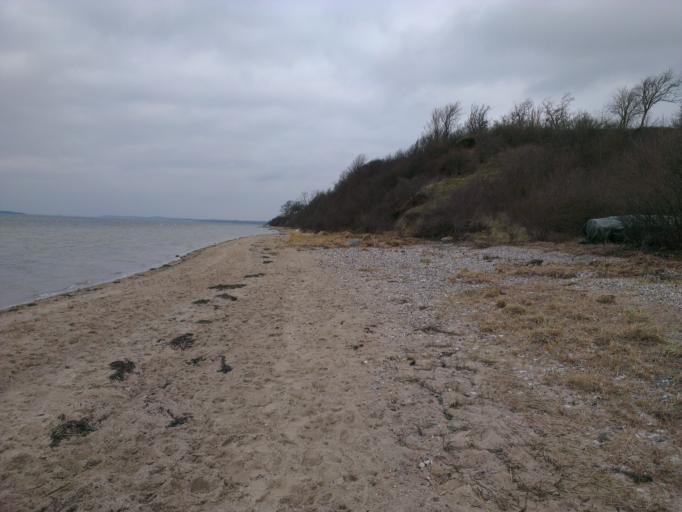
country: DK
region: Capital Region
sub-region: Frederikssund Kommune
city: Frederikssund
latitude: 55.8523
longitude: 12.0445
